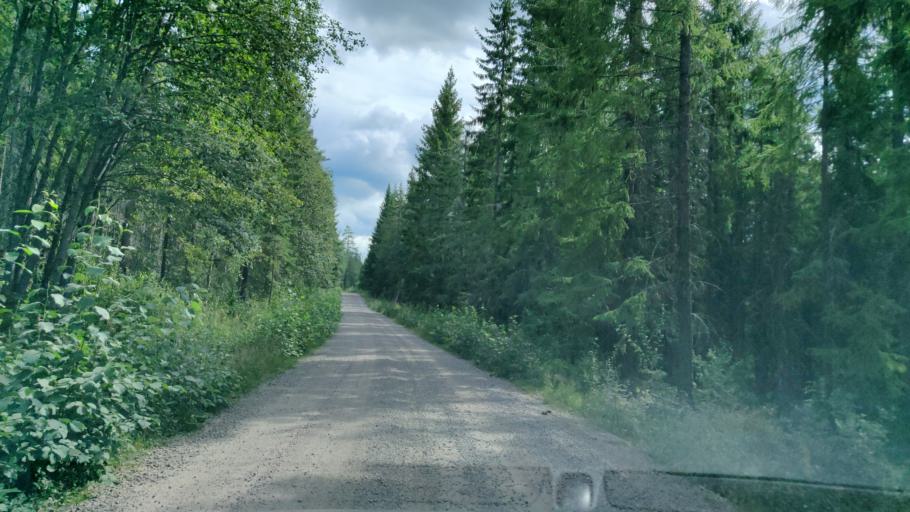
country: SE
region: Vaermland
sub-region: Hagfors Kommun
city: Hagfors
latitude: 60.0088
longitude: 13.7099
